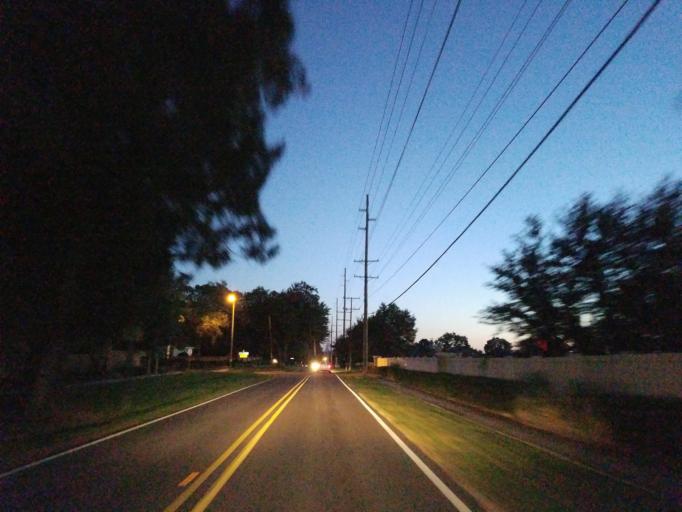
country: US
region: Florida
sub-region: Hillsborough County
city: Bloomingdale
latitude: 27.9026
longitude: -82.2278
